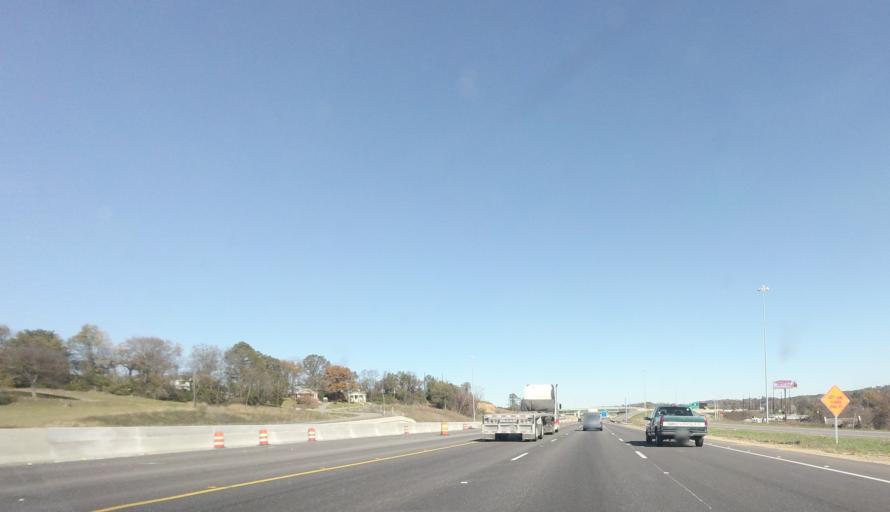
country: US
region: Alabama
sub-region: Jefferson County
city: Birmingham
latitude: 33.5650
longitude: -86.8241
